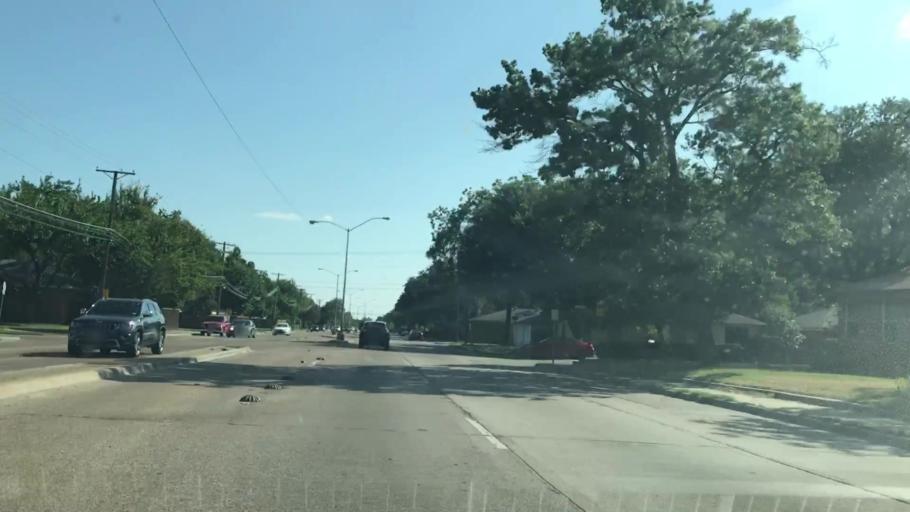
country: US
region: Texas
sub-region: Dallas County
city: Garland
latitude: 32.8310
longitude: -96.6752
